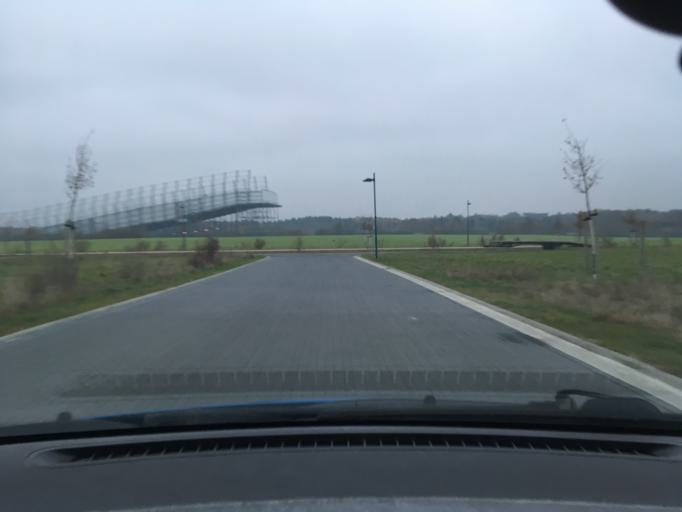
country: DE
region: Lower Saxony
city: Bispingen
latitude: 53.0988
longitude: 9.9866
